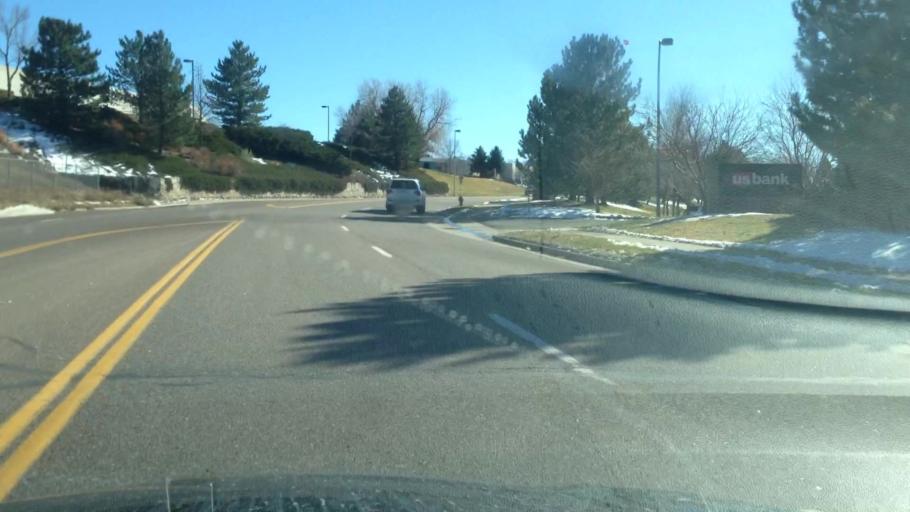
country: US
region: Colorado
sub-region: Arapahoe County
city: Centennial
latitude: 39.5823
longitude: -104.8572
